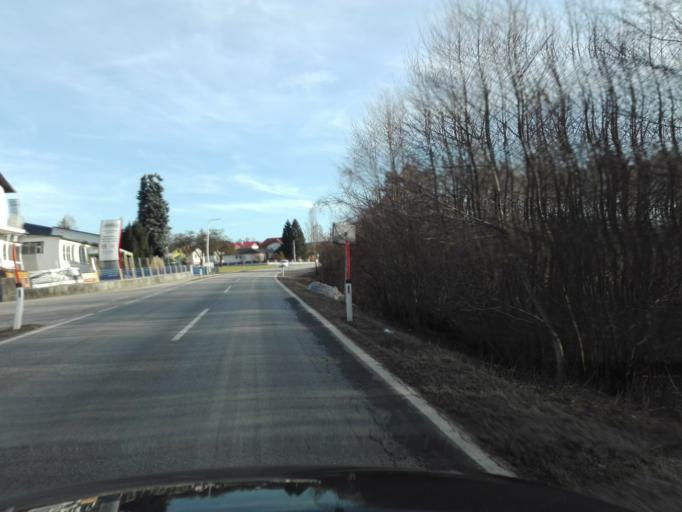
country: AT
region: Lower Austria
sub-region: Politischer Bezirk Amstetten
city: Amstetten
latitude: 48.1715
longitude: 14.8365
